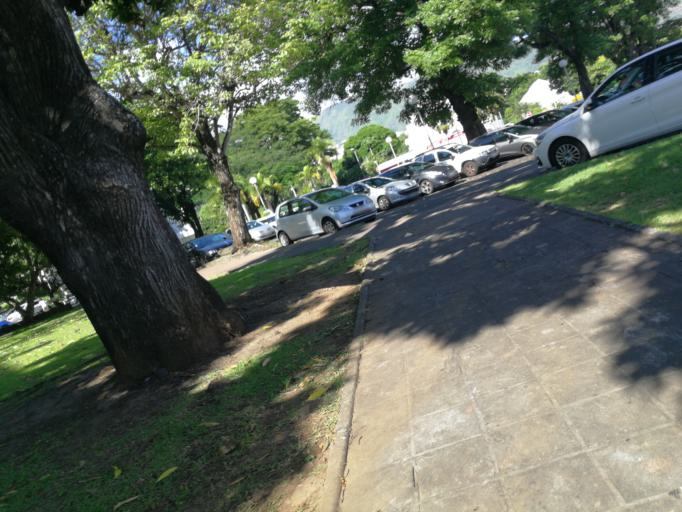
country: RE
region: Reunion
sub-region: Reunion
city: Saint-Denis
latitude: -20.8860
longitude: 55.4668
